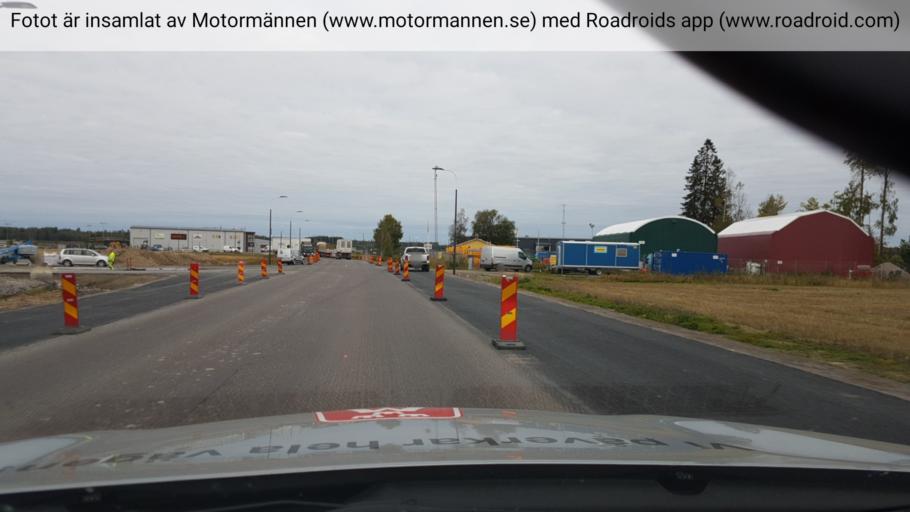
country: SE
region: Uppsala
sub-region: Tierps Kommun
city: Tierp
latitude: 60.3446
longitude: 17.4948
